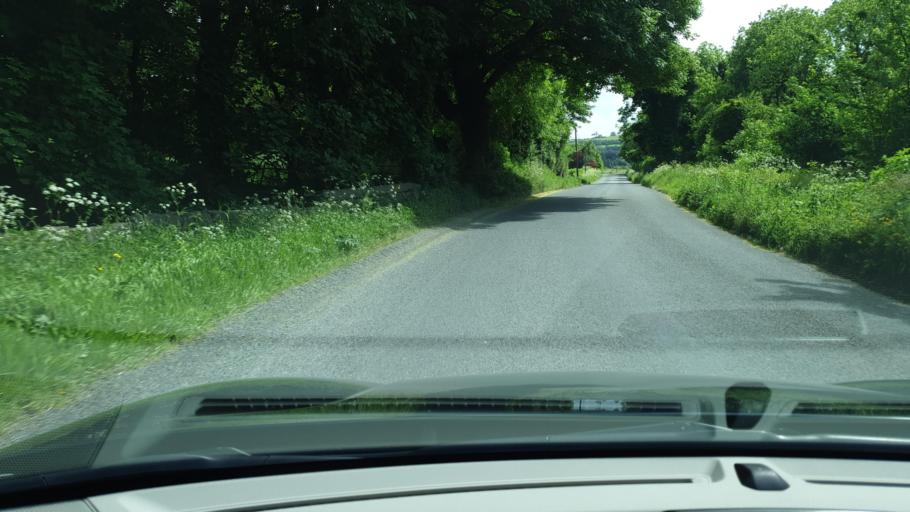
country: IE
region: Leinster
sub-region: An Mhi
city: Slane
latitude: 53.7206
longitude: -6.5742
